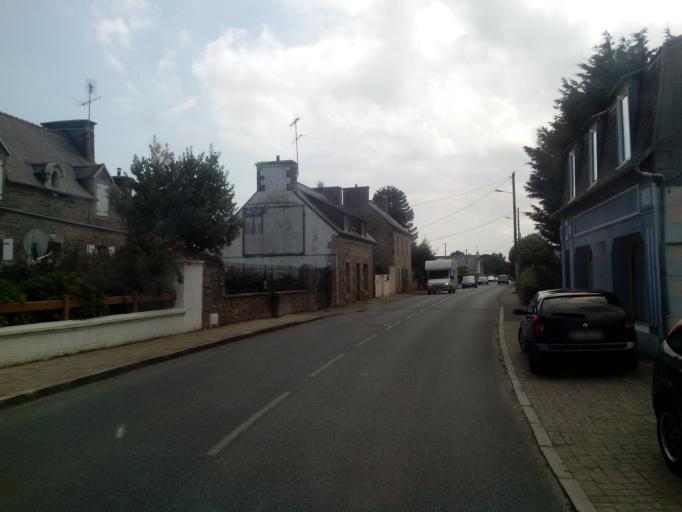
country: FR
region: Brittany
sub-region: Departement des Cotes-d'Armor
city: Plouezec
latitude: 48.7473
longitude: -2.9841
